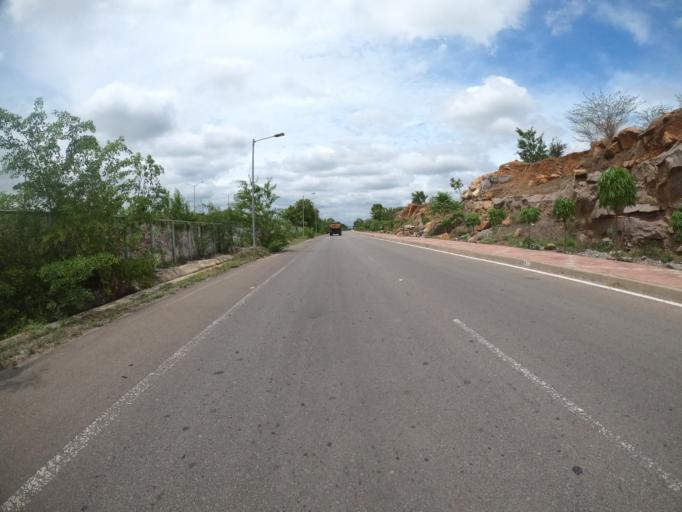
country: IN
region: Telangana
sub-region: Rangareddi
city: Balapur
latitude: 17.2755
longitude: 78.3814
